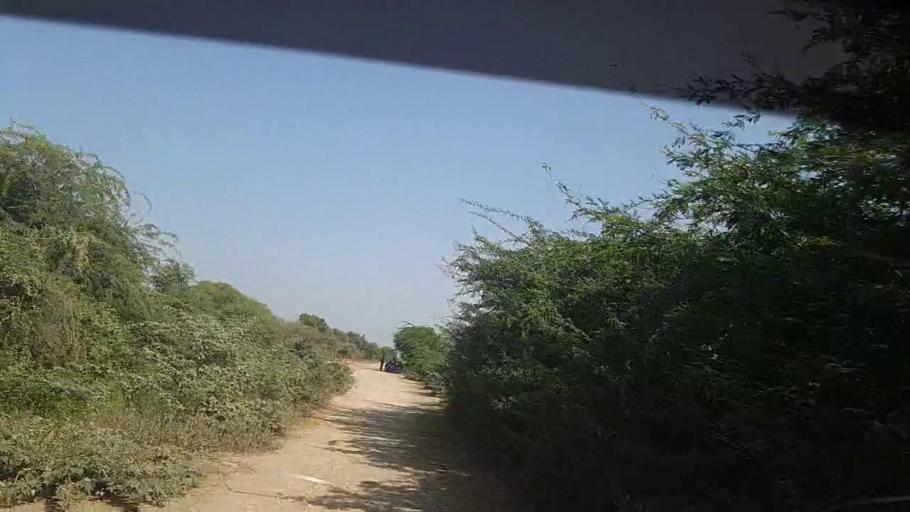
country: PK
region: Sindh
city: Rajo Khanani
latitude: 24.9683
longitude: 68.8804
